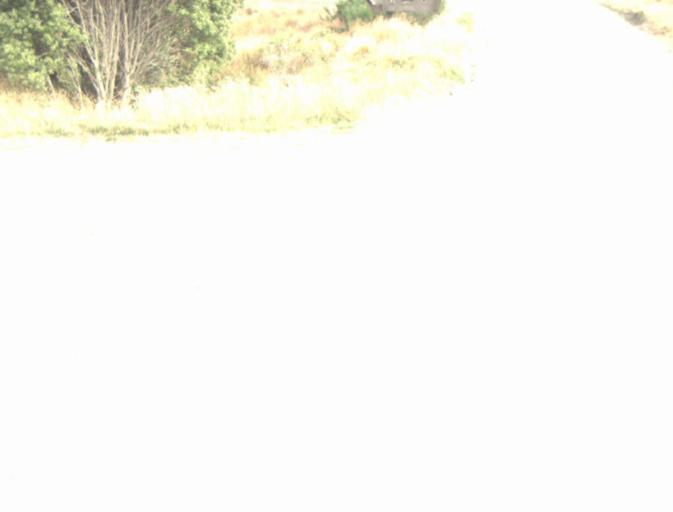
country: AU
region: Tasmania
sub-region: Dorset
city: Scottsdale
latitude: -41.3537
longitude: 147.4548
